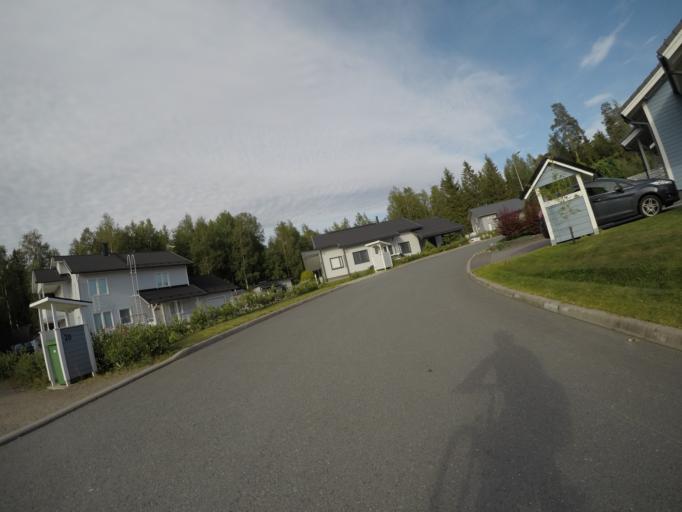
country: FI
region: Haeme
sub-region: Haemeenlinna
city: Parola
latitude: 60.9768
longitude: 24.3850
